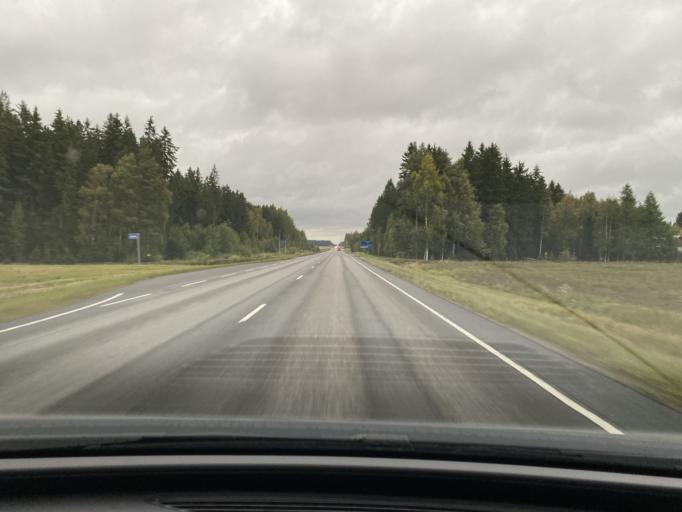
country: FI
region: Satakunta
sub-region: Pori
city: Vampula
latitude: 61.0344
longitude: 22.6612
